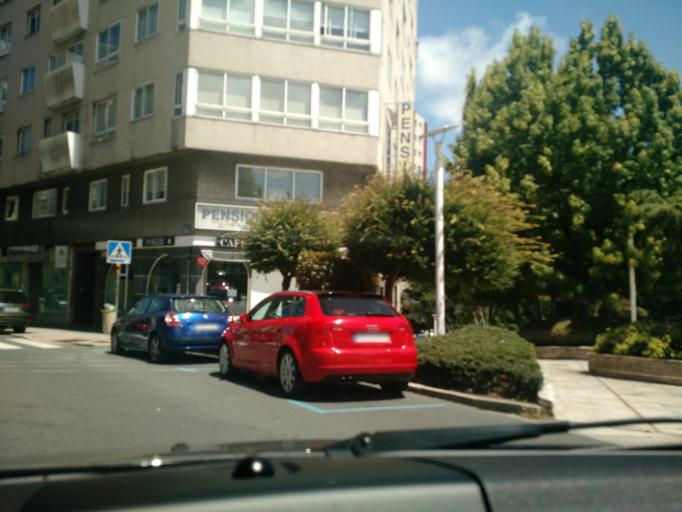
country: ES
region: Galicia
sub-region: Provincia da Coruna
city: A Coruna
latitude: 43.3545
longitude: -8.4053
